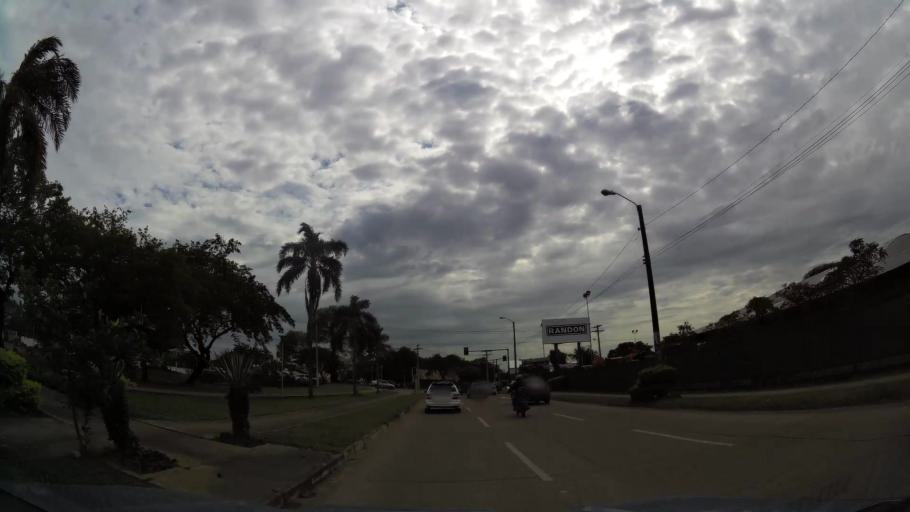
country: BO
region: Santa Cruz
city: Santa Cruz de la Sierra
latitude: -17.7609
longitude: -63.1911
